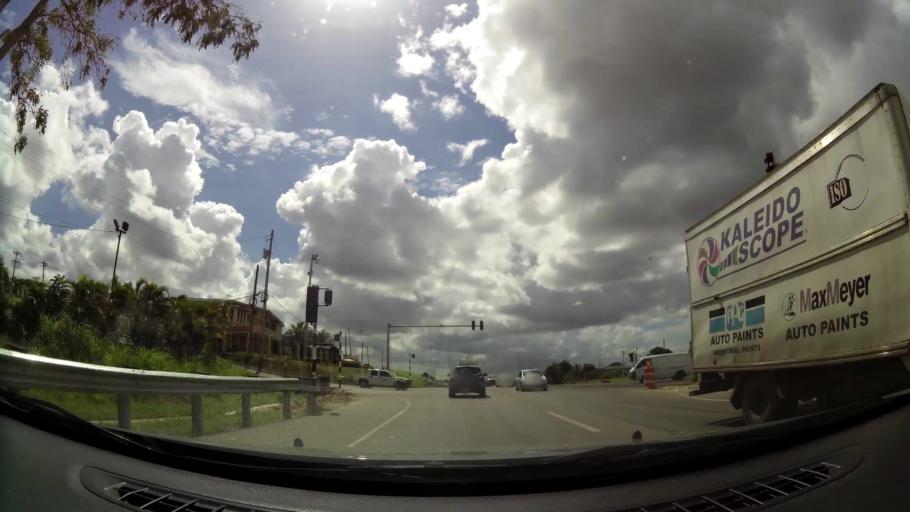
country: TT
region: City of San Fernando
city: San Fernando
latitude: 10.2528
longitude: -61.4828
